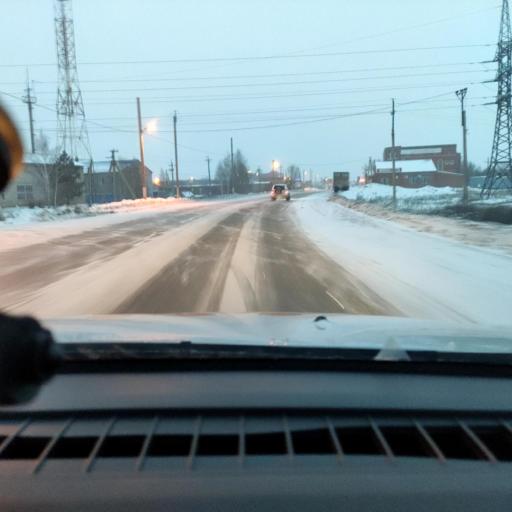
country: RU
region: Samara
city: Kinel'-Cherkassy
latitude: 53.4543
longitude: 51.5159
